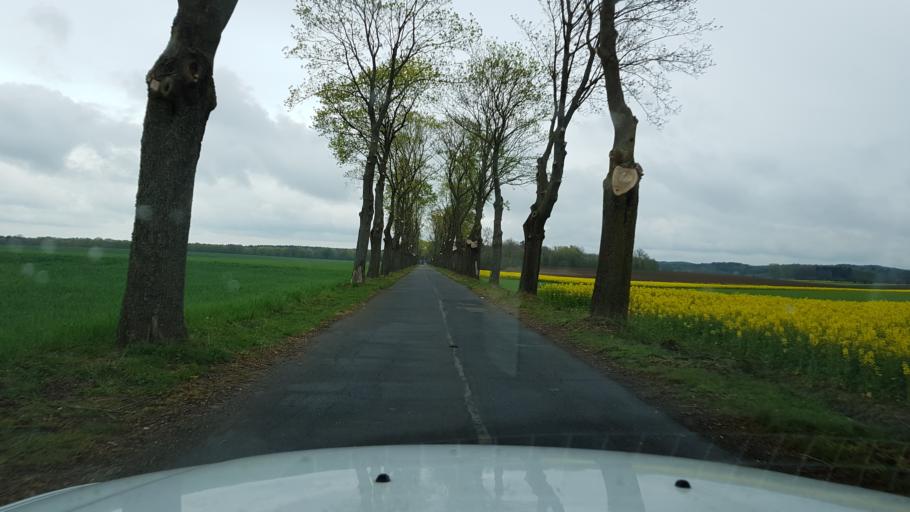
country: PL
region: West Pomeranian Voivodeship
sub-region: Powiat gryficki
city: Brojce
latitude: 53.9432
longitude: 15.4230
